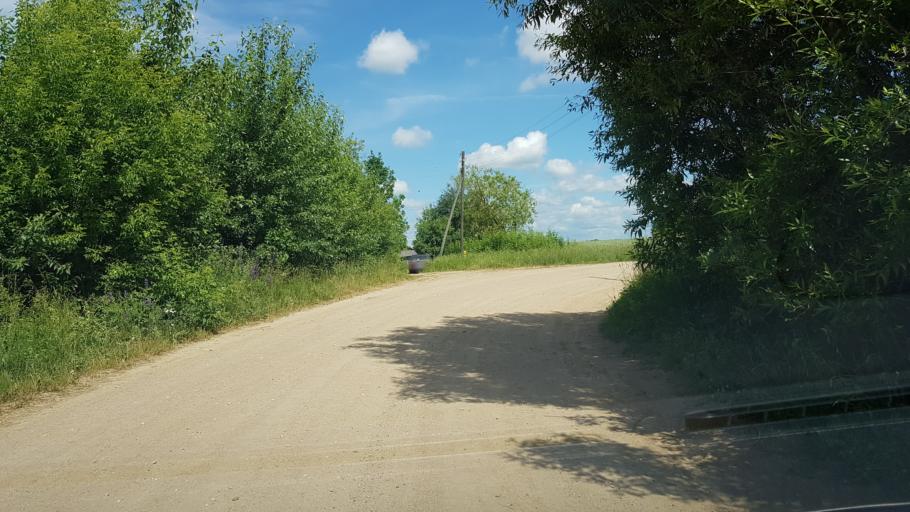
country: BY
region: Vitebsk
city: Dubrowna
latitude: 54.4888
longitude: 30.7955
